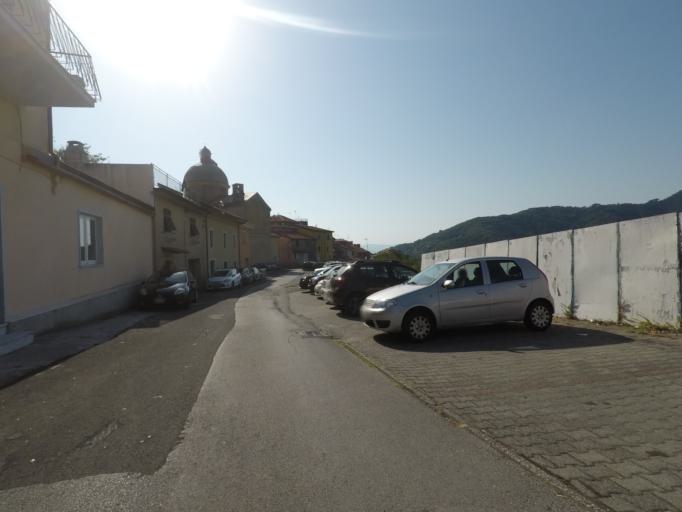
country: IT
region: Liguria
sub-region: Provincia di La Spezia
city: Casano-Dogana-Isola
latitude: 44.0892
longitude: 10.0552
